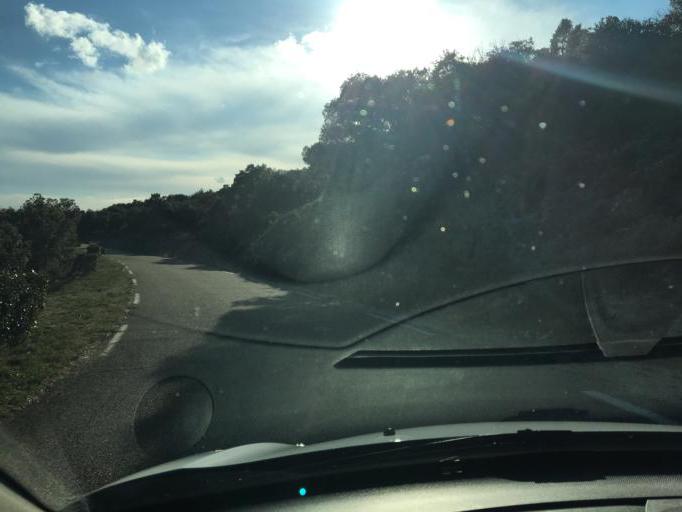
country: FR
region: Provence-Alpes-Cote d'Azur
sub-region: Departement du Vaucluse
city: Villes-sur-Auzon
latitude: 44.0447
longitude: 5.2543
